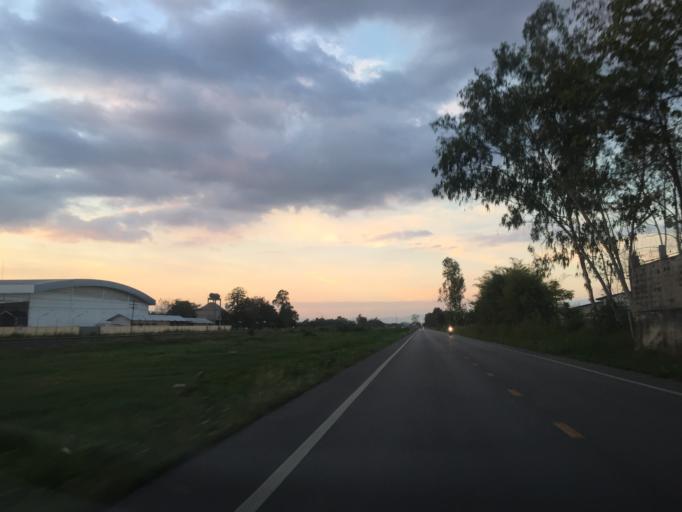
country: TH
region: Lamphun
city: Lamphun
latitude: 18.5598
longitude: 99.0422
